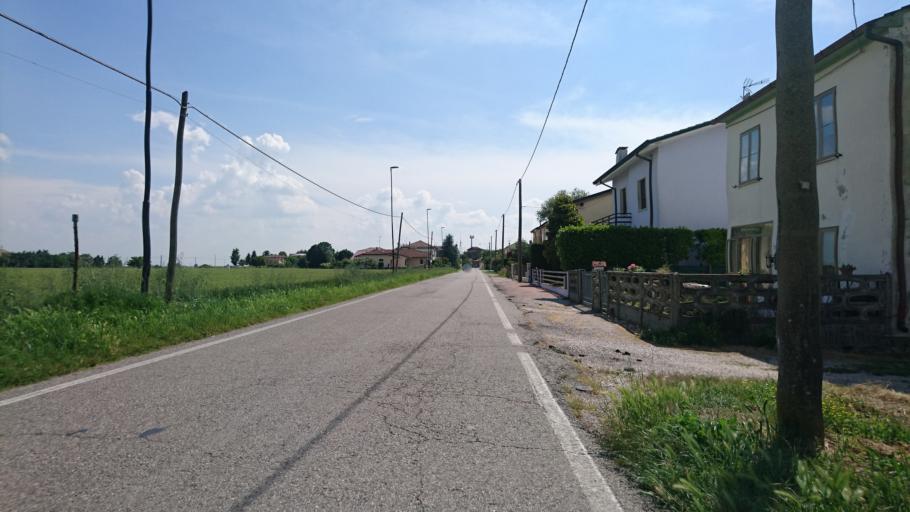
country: IT
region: Veneto
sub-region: Provincia di Rovigo
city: Castelmassa
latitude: 45.0617
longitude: 11.3333
